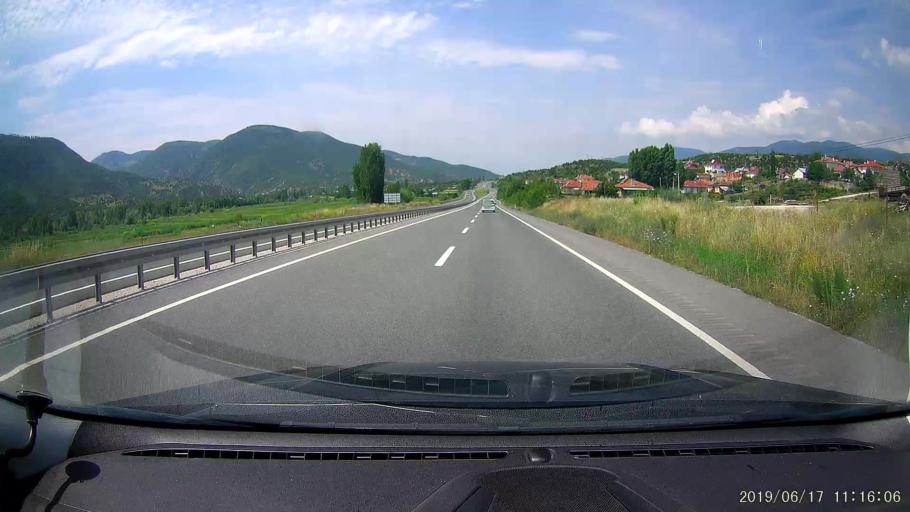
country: TR
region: Kastamonu
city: Tosya
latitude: 40.9484
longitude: 33.9070
